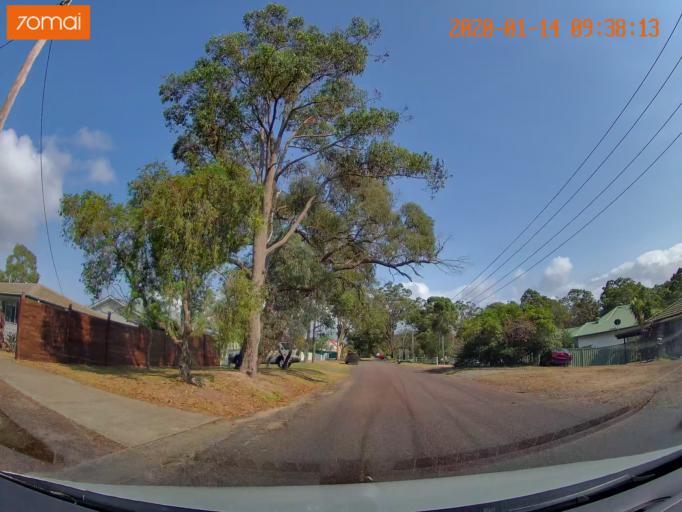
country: AU
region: New South Wales
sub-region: Wyong Shire
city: Kingfisher Shores
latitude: -33.1122
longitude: 151.5569
